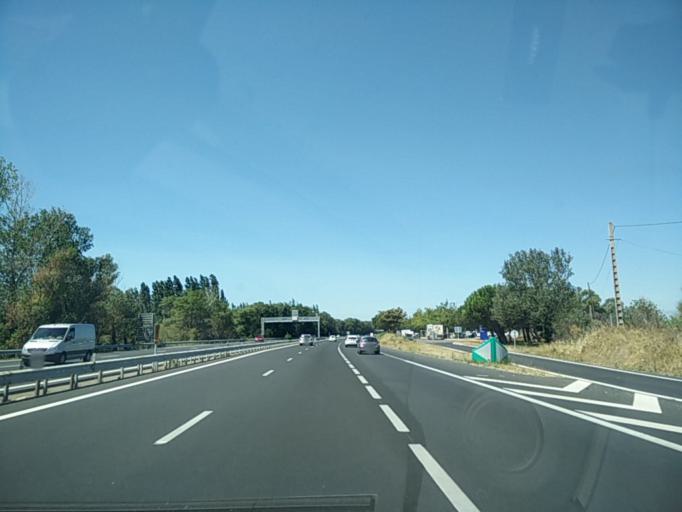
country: FR
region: Provence-Alpes-Cote d'Azur
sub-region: Departement du Vaucluse
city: Cavaillon
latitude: 43.8312
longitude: 5.0116
